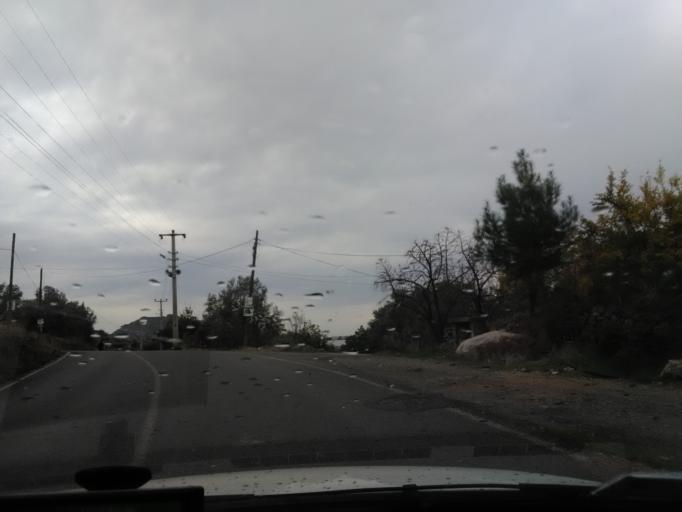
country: TR
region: Antalya
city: Gazipasa
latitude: 36.2589
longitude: 32.3133
